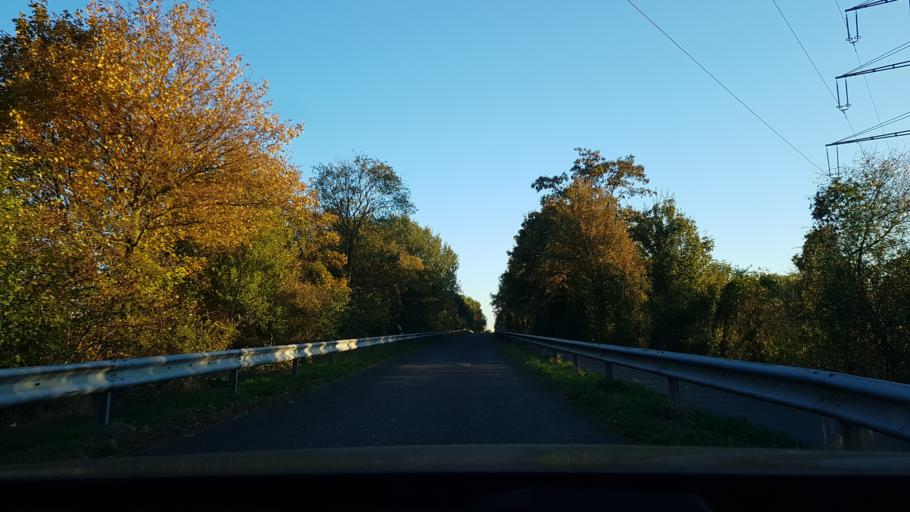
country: DE
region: North Rhine-Westphalia
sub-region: Regierungsbezirk Dusseldorf
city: Moers
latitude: 51.4350
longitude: 6.5815
